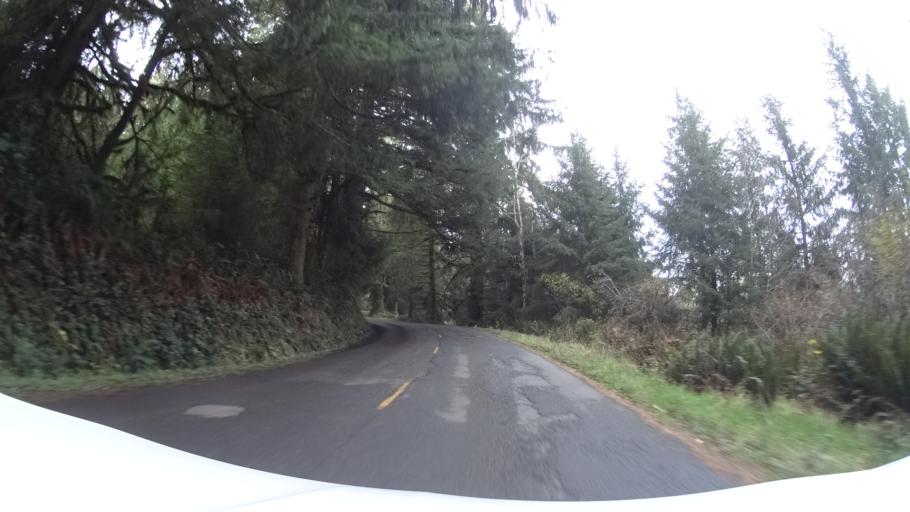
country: US
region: California
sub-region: Humboldt County
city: Ferndale
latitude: 40.5381
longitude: -124.2765
